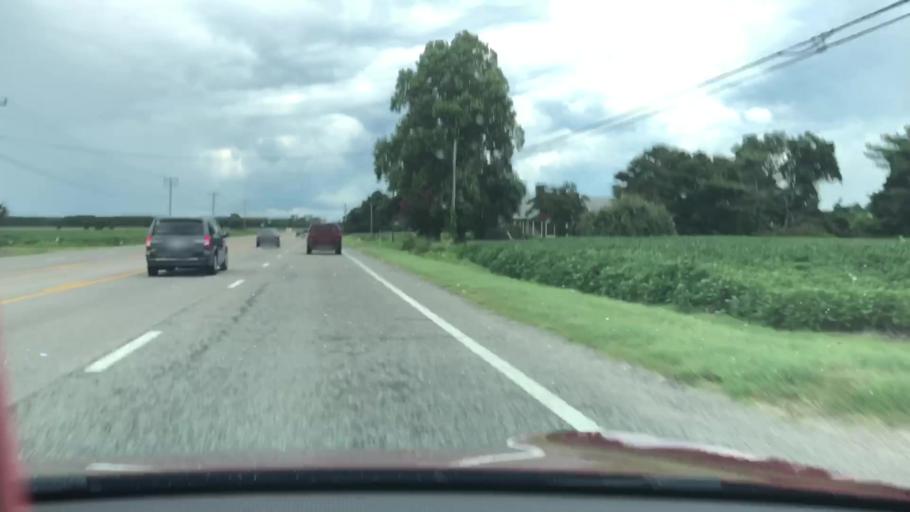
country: US
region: North Carolina
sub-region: Dare County
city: Southern Shores
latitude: 36.1882
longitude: -75.8637
